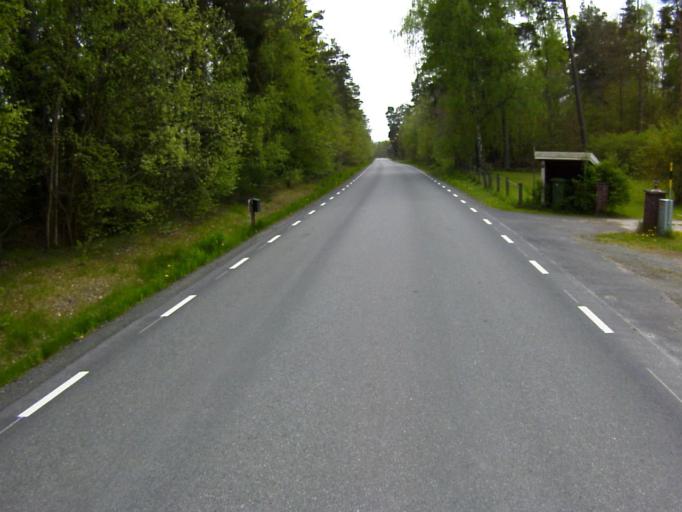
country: SE
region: Skane
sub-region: Kristianstads Kommun
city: Onnestad
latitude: 55.9448
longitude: 13.9803
